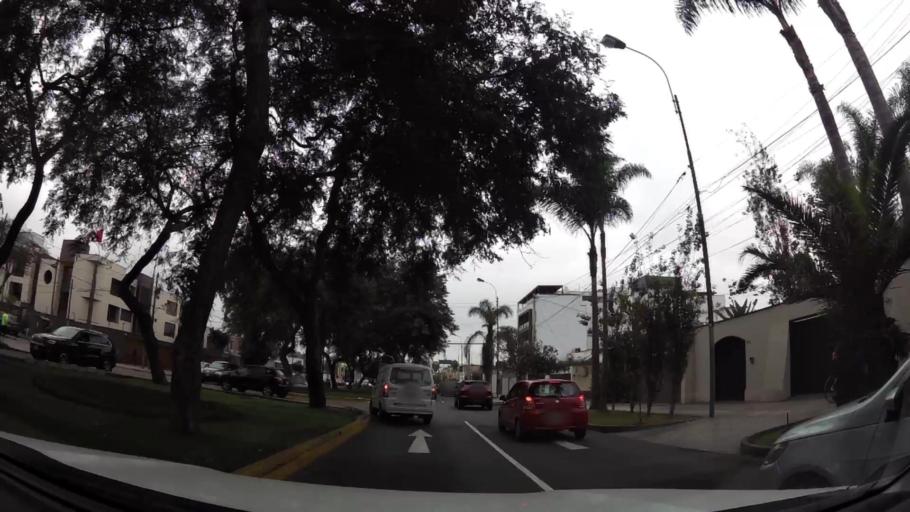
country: PE
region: Lima
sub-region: Lima
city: San Luis
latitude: -12.1094
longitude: -76.9847
